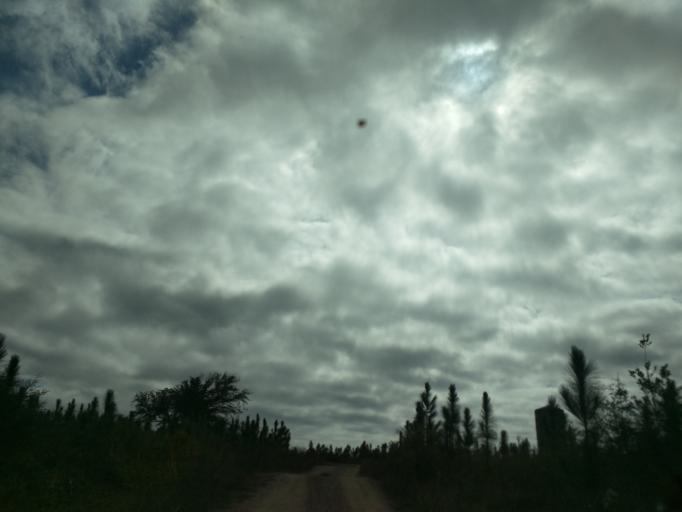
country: US
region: Florida
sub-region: Escambia County
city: Cantonment
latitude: 30.5400
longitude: -87.4309
